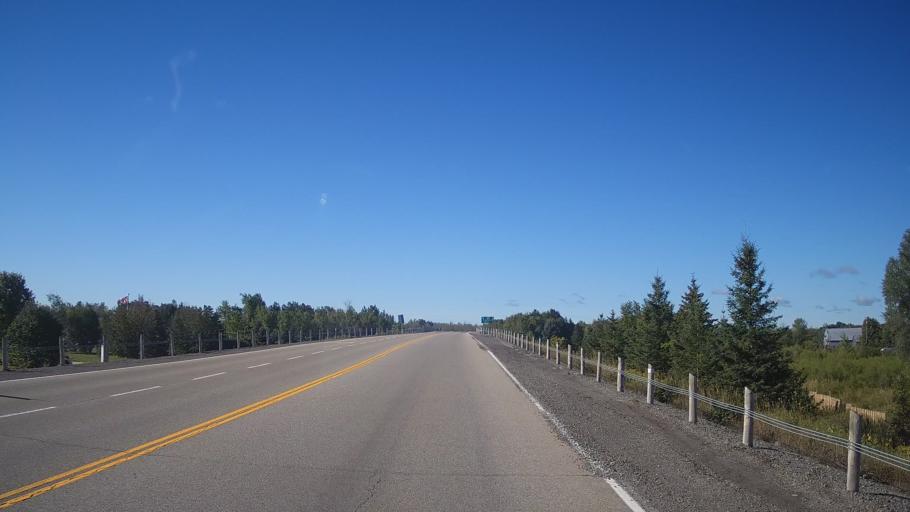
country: CA
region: Ontario
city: Bells Corners
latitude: 45.0829
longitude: -75.6324
